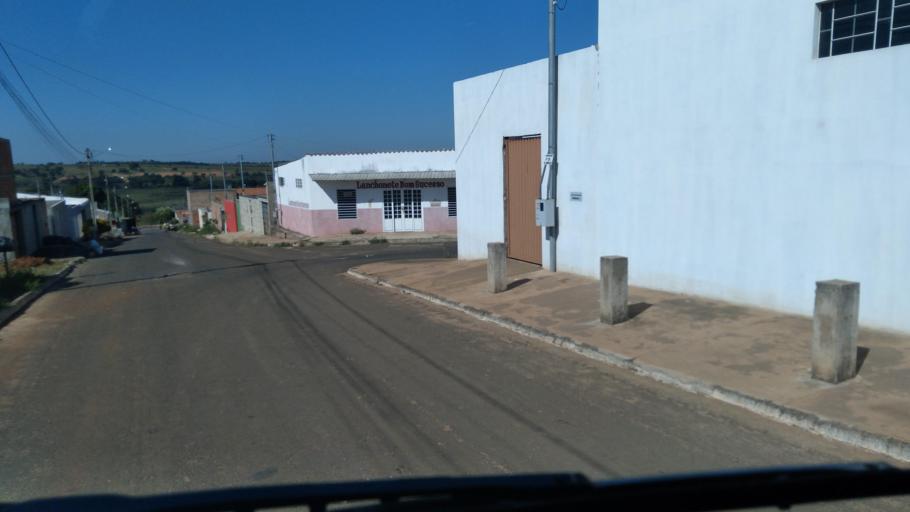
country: BR
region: Goias
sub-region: Mineiros
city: Mineiros
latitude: -17.5753
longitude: -52.5754
